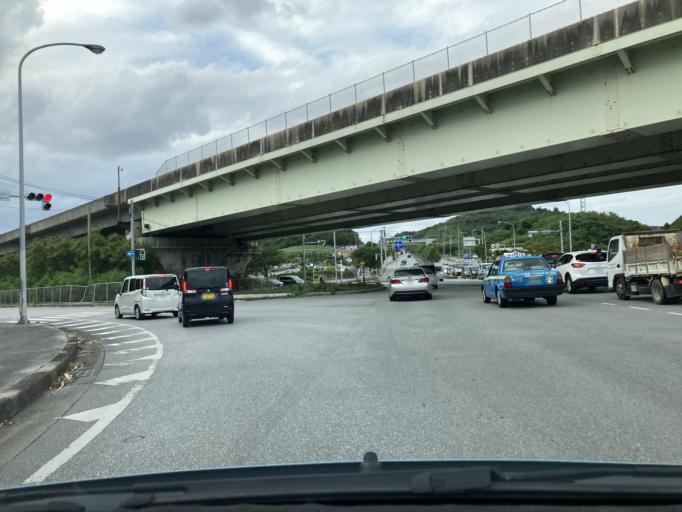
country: JP
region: Okinawa
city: Tomigusuku
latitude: 26.1806
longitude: 127.7245
